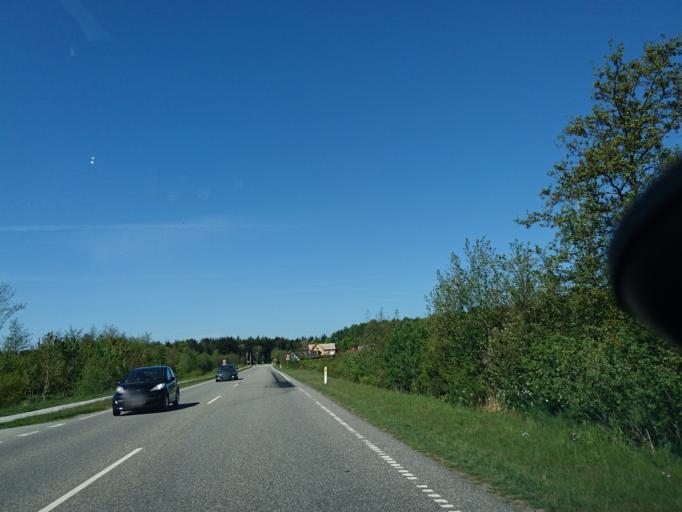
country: DK
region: North Denmark
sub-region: Hjorring Kommune
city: Sindal
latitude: 57.4708
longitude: 10.2236
